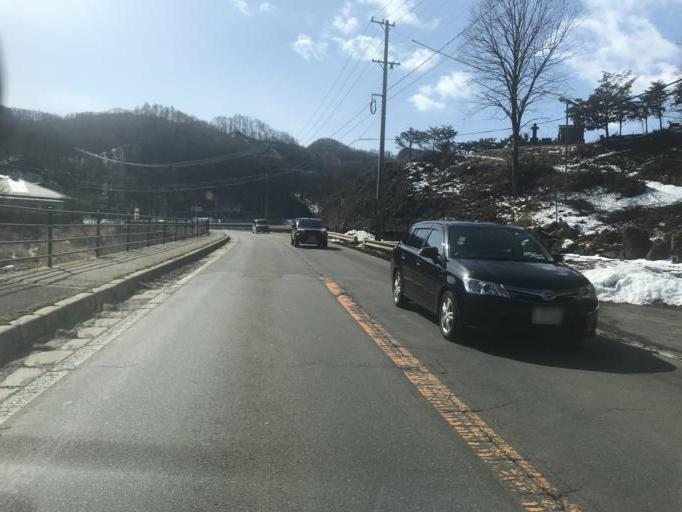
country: JP
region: Nagano
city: Saku
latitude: 36.0098
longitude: 138.4937
